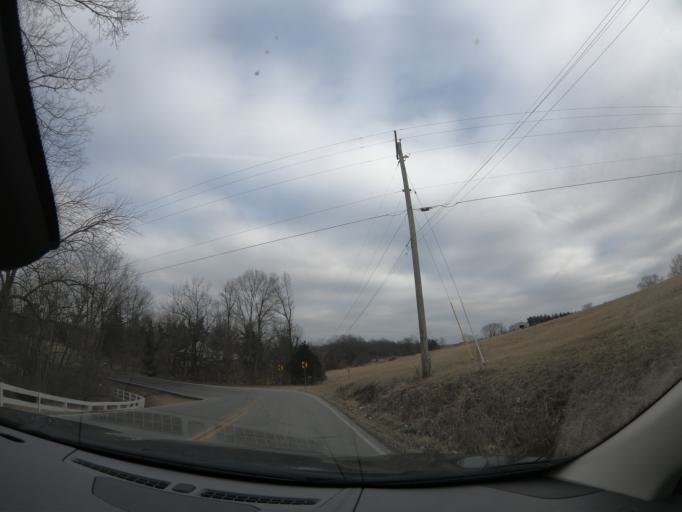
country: US
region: Kentucky
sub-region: Spencer County
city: Taylorsville
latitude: 37.9217
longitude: -85.3165
